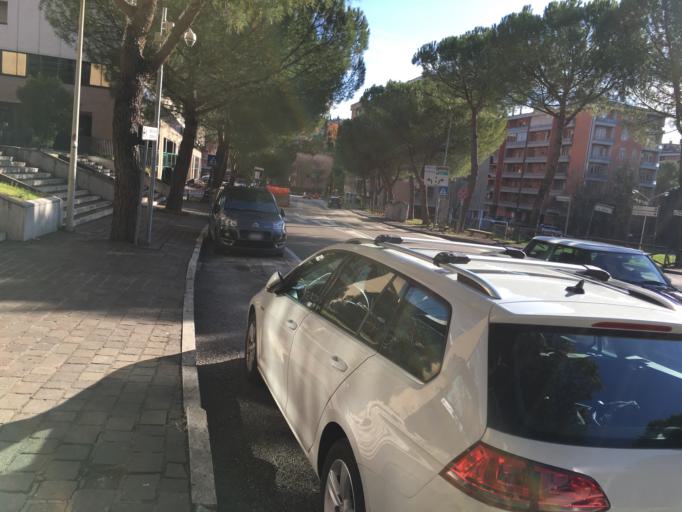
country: IT
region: Umbria
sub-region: Provincia di Perugia
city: Perugia
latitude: 43.1020
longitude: 12.3729
